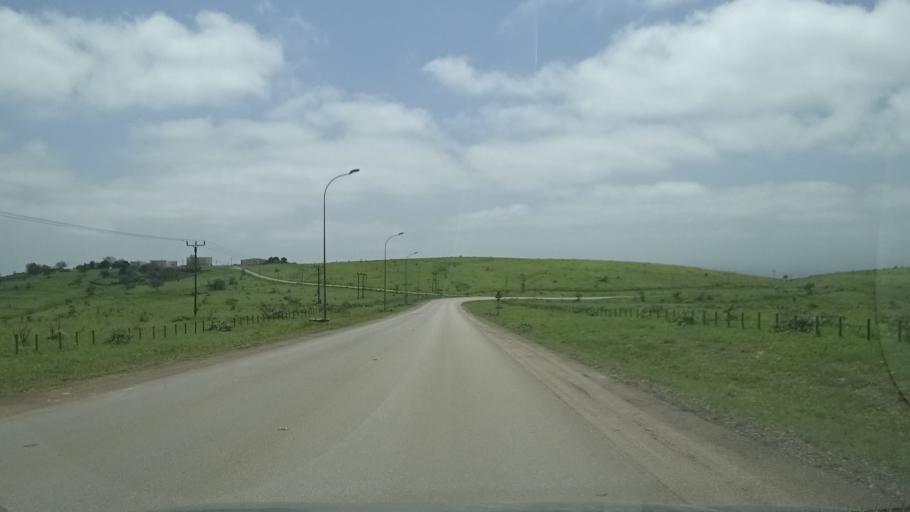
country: OM
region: Zufar
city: Salalah
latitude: 17.1724
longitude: 54.2374
